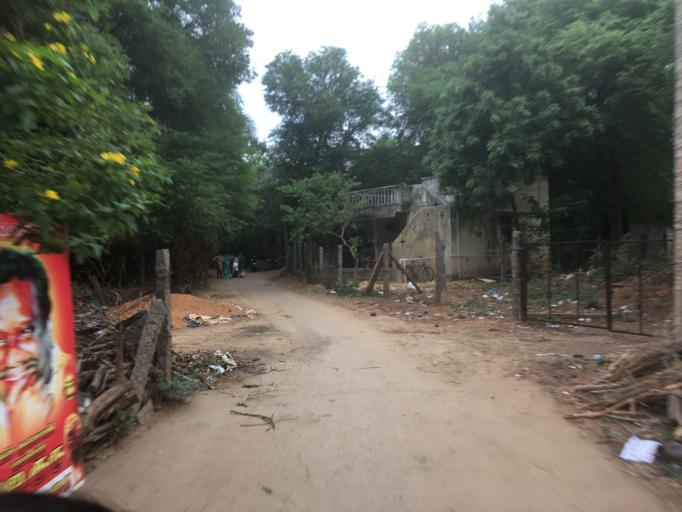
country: IN
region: Tamil Nadu
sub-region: Villupuram
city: Auroville
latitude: 12.0097
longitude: 79.8018
